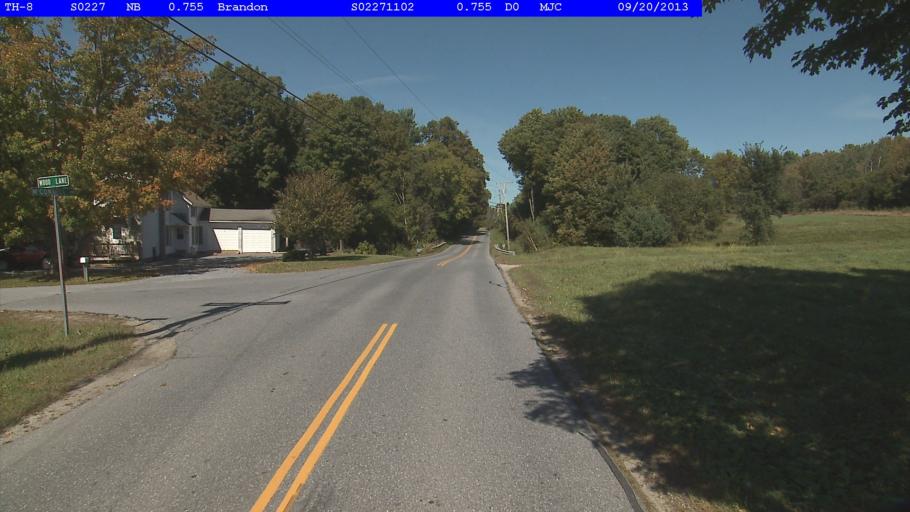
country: US
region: Vermont
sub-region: Rutland County
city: Brandon
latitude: 43.7853
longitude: -73.0534
